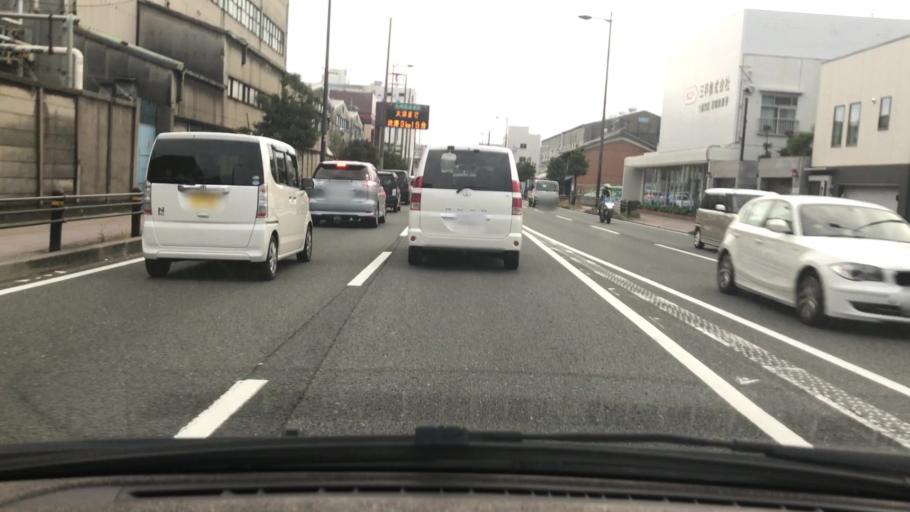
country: JP
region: Kyoto
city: Muko
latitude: 34.9685
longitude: 135.7460
